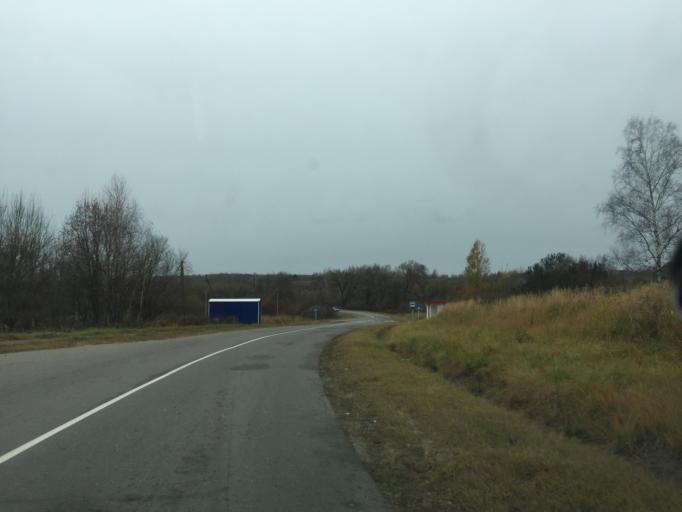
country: BY
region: Mogilev
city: Chavusy
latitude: 53.9026
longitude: 31.0554
